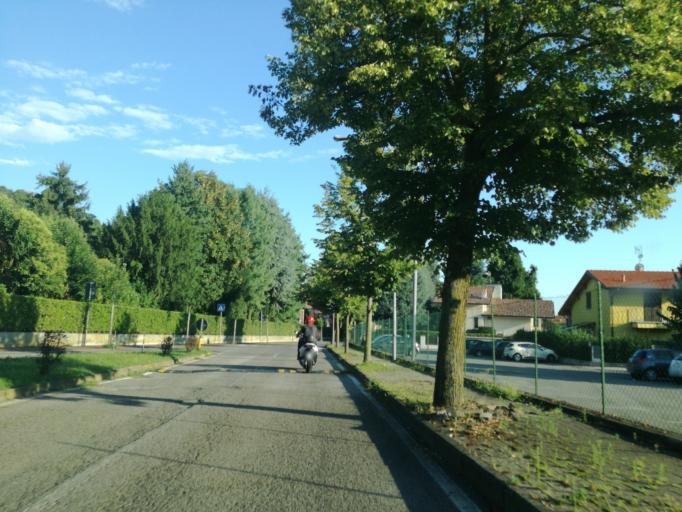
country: IT
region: Lombardy
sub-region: Provincia di Lecco
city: Robbiate
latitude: 45.6946
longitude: 9.4409
